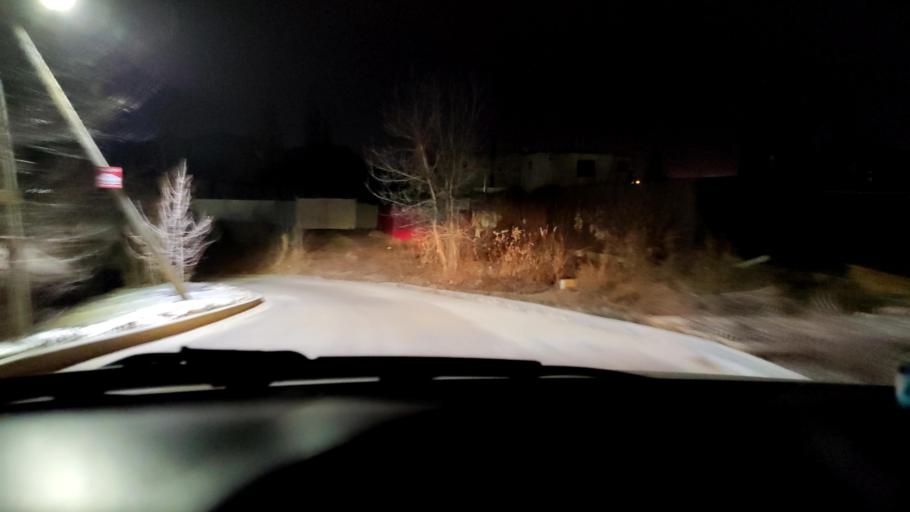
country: RU
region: Voronezj
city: Voronezh
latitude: 51.6325
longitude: 39.1582
